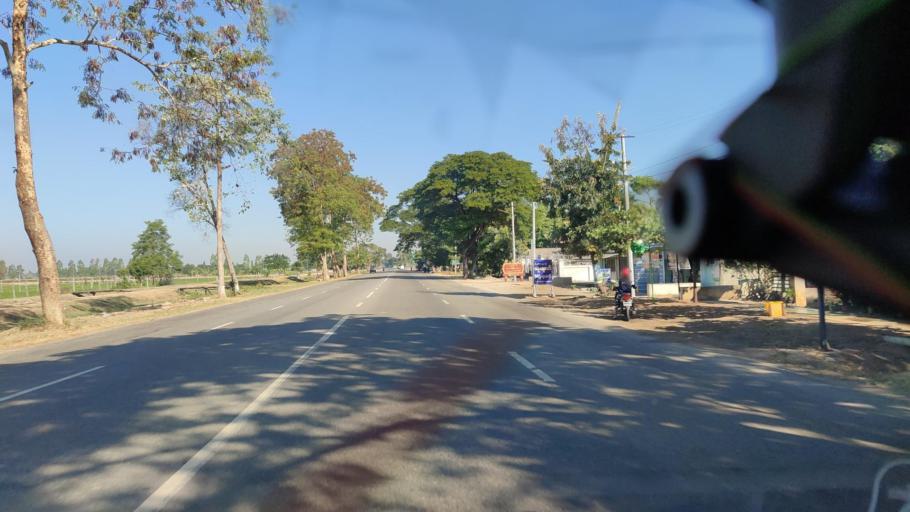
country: MM
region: Mandalay
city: Pyinmana
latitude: 19.7922
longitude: 96.2621
